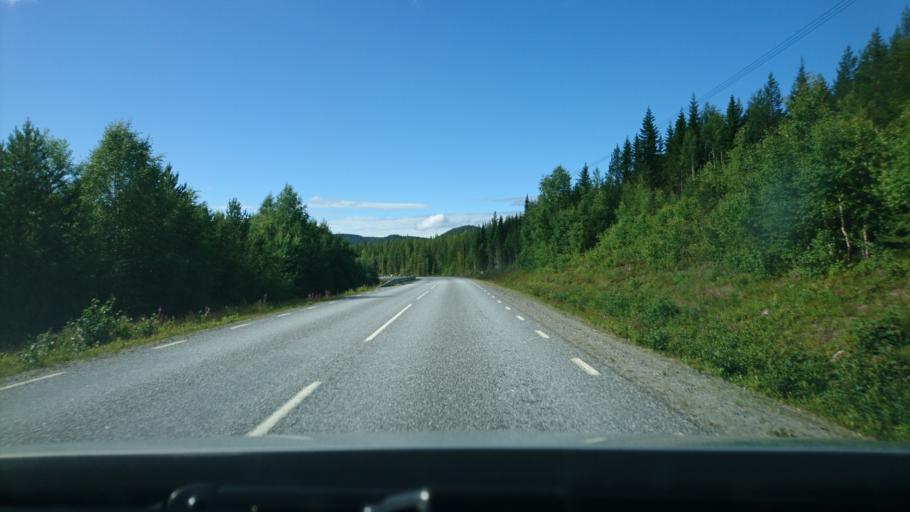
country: SE
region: Vaesterbotten
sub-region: Asele Kommun
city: Asele
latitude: 64.3175
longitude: 17.2129
